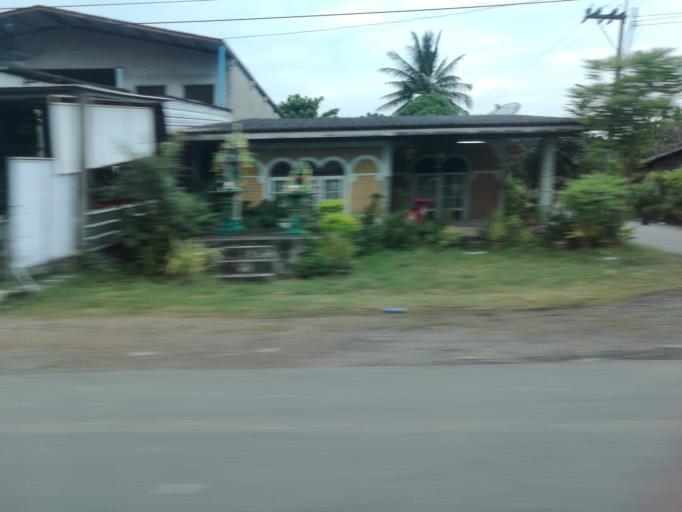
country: TH
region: Prachuap Khiri Khan
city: Pran Buri
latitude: 12.3399
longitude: 99.8815
